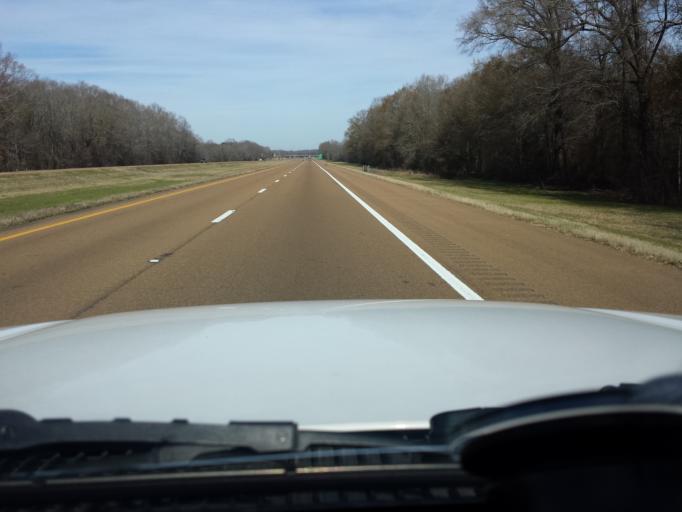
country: US
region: Mississippi
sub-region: Madison County
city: Canton
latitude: 32.6551
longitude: -90.0619
